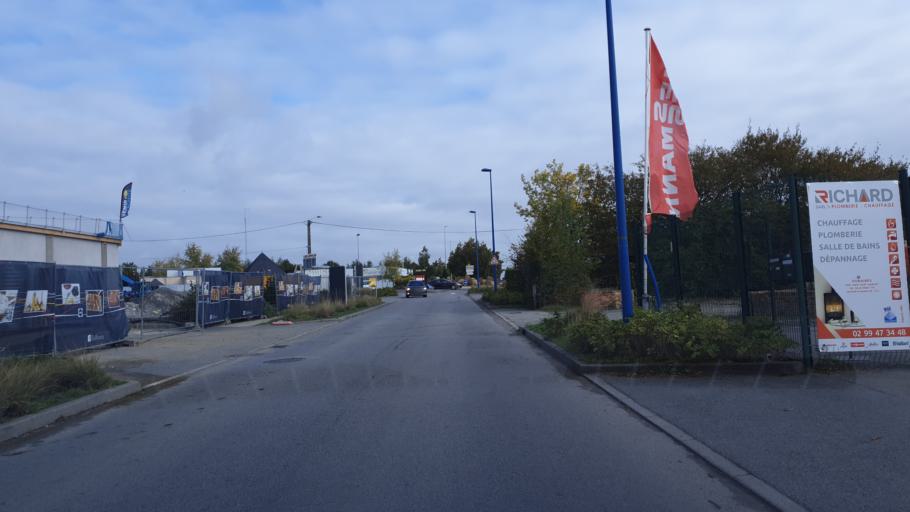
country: FR
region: Brittany
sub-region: Departement d'Ille-et-Vilaine
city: Janze
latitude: 47.9564
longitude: -1.4899
